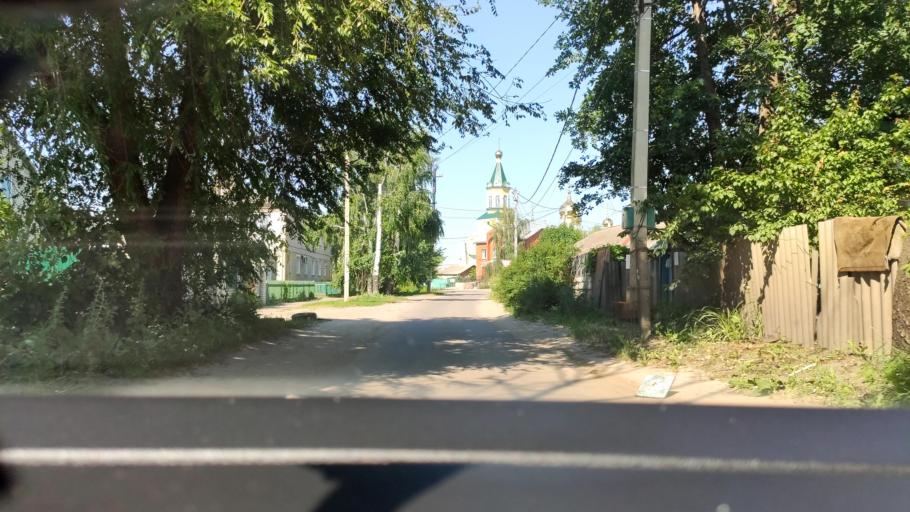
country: RU
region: Voronezj
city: Novaya Usman'
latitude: 51.6411
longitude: 39.4106
